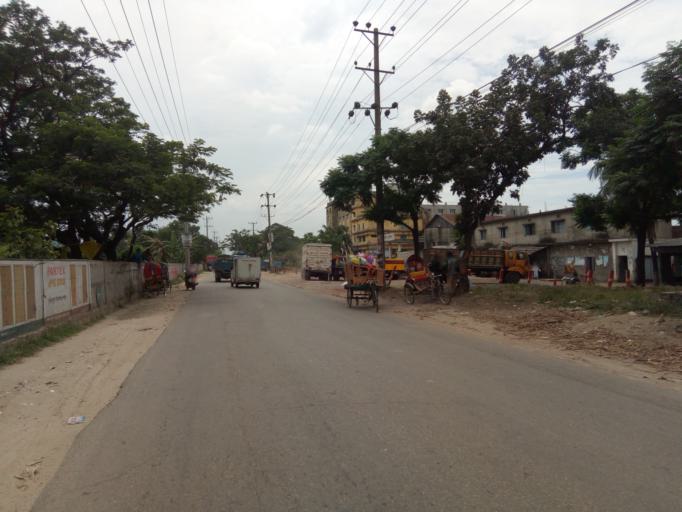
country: BD
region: Dhaka
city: Paltan
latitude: 23.7170
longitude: 90.4703
